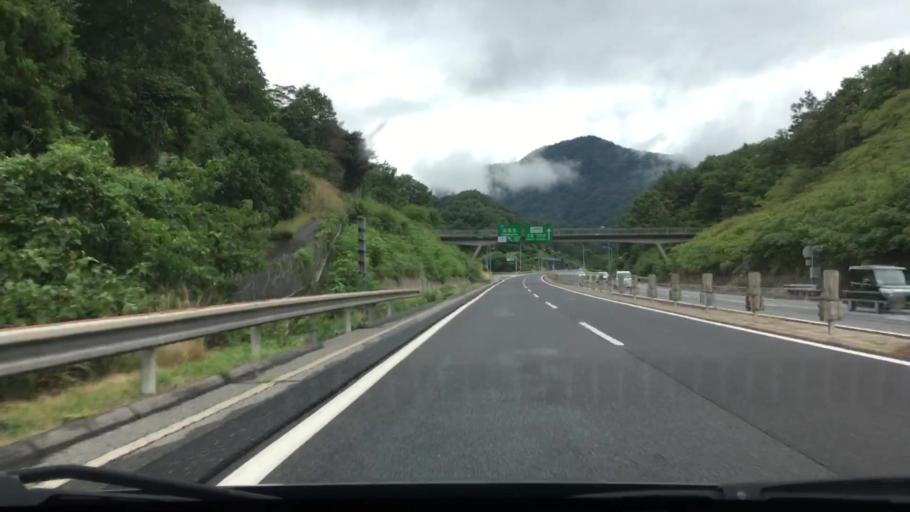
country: JP
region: Hiroshima
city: Hiroshima-shi
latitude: 34.5546
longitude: 132.4511
